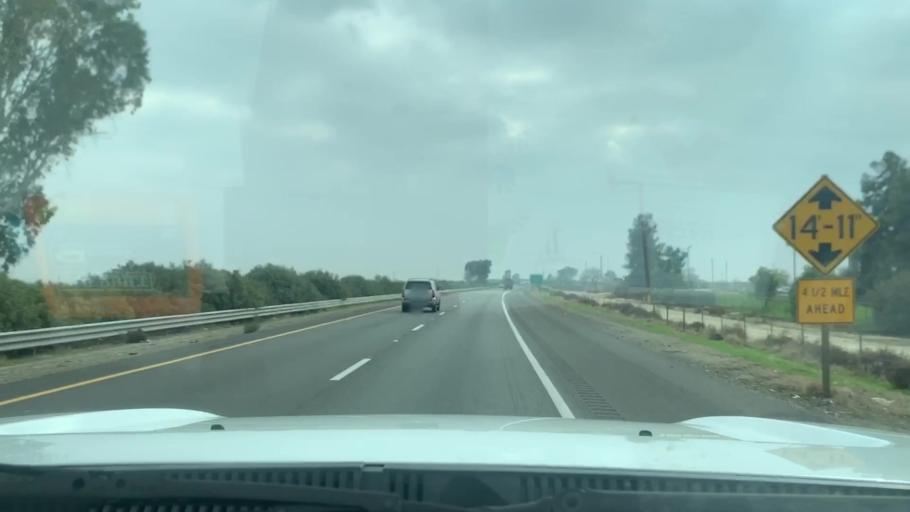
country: US
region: California
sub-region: Tulare County
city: Tipton
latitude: 36.1323
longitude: -119.3258
